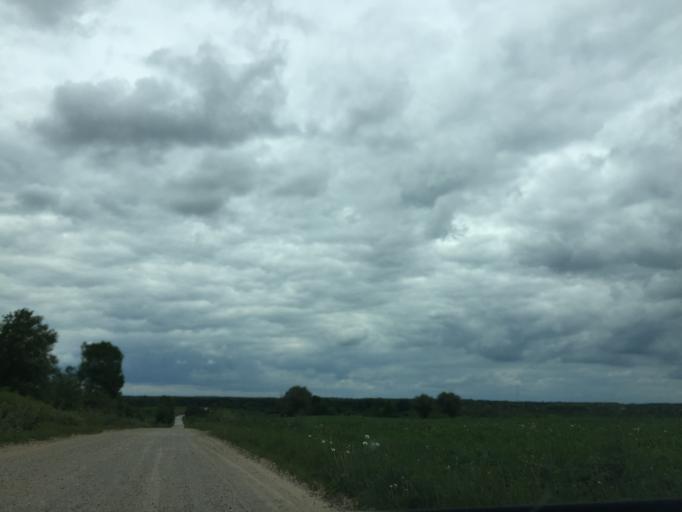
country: LV
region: Dagda
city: Dagda
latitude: 56.0156
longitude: 27.5997
